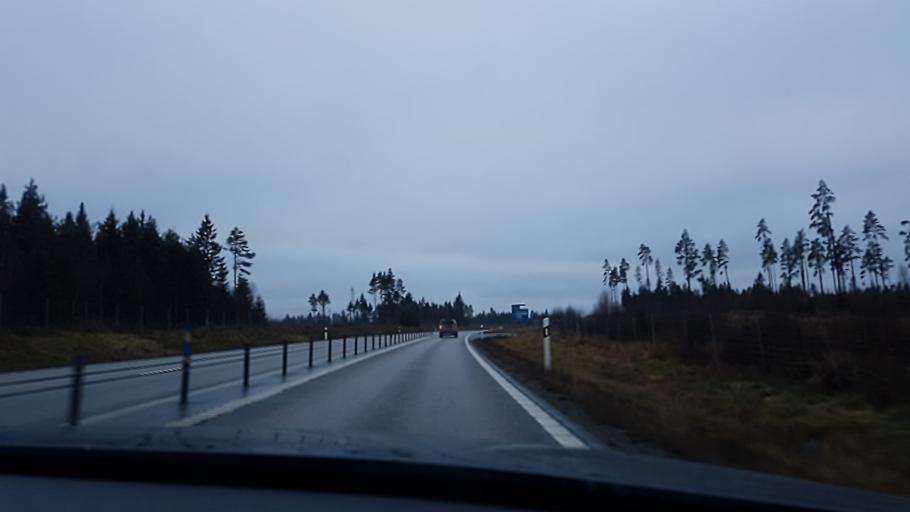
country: SE
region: Kronoberg
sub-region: Ljungby Kommun
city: Lagan
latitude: 56.9709
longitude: 14.0173
